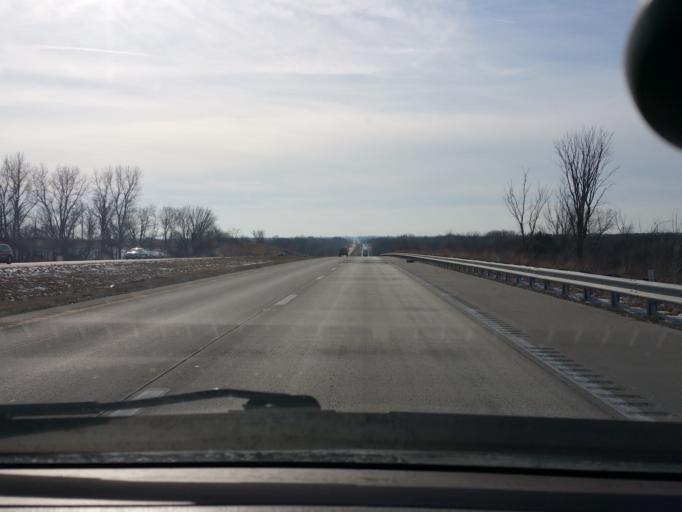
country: US
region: Missouri
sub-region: Clay County
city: Kearney
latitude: 39.4219
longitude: -94.3430
